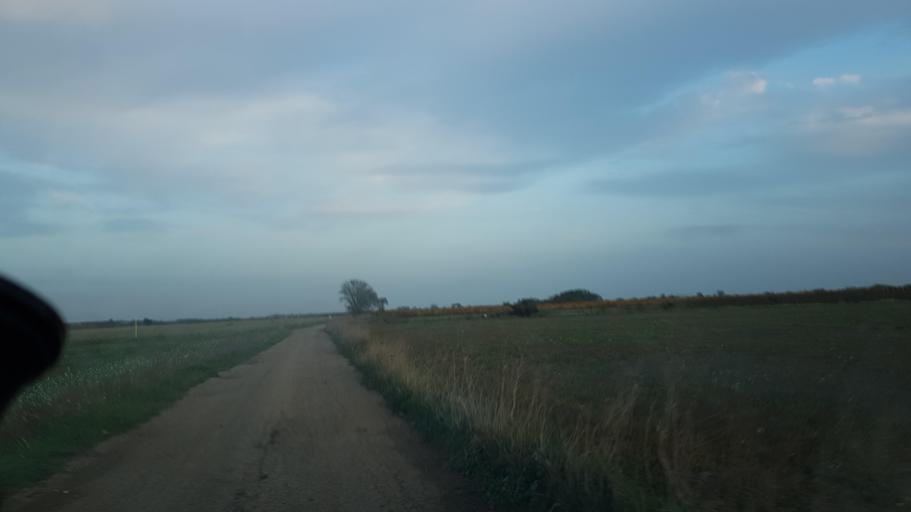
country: IT
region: Apulia
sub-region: Provincia di Brindisi
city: San Donaci
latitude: 40.4267
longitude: 17.9172
